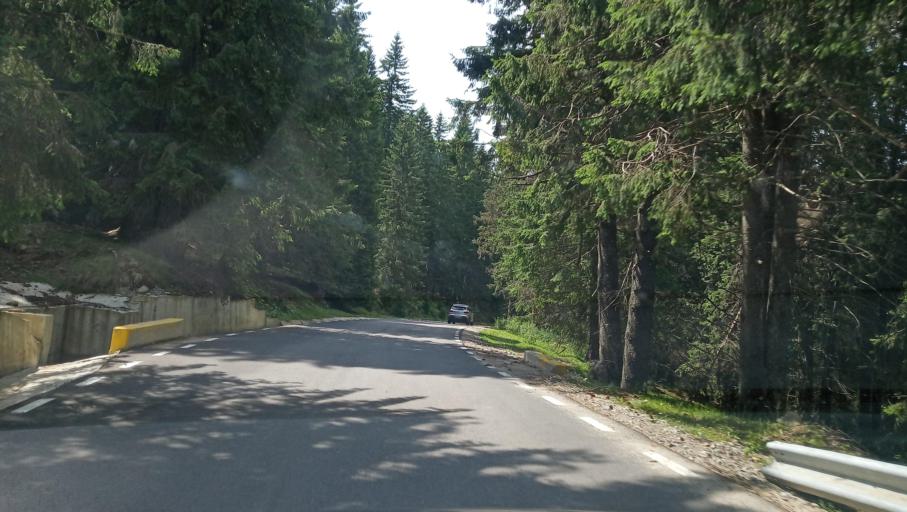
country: RO
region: Dambovita
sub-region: Comuna Moroeni
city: Glod
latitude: 45.3250
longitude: 25.4582
